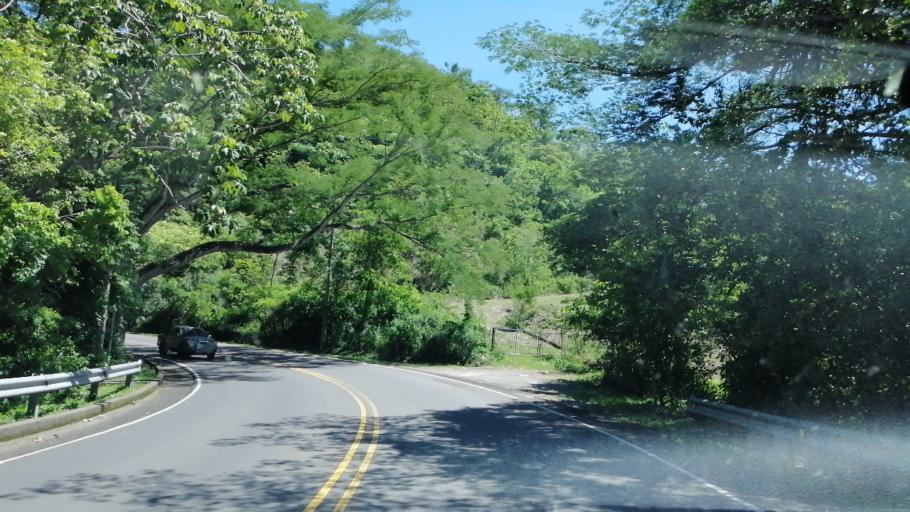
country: SV
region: Morazan
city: Cacaopera
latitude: 13.8002
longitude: -88.1479
